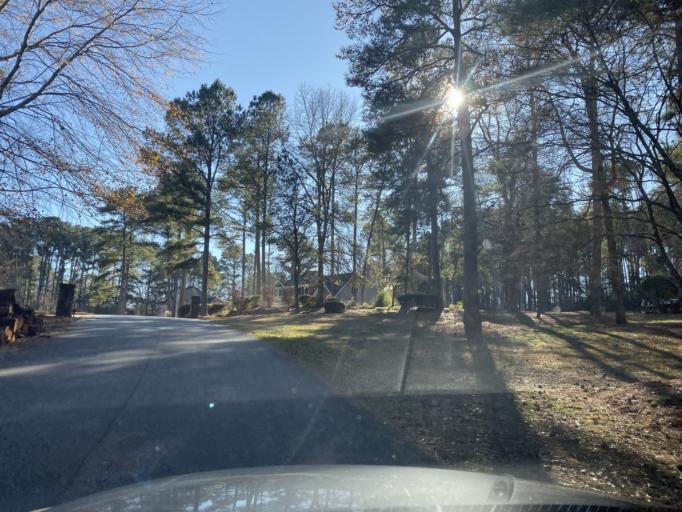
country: US
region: Georgia
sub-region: DeKalb County
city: Pine Mountain
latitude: 33.6815
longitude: -84.1661
